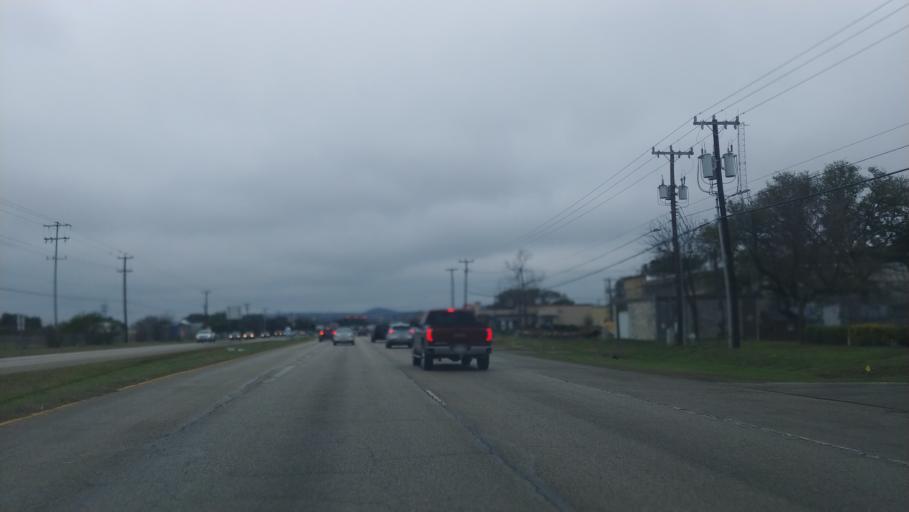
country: US
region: Texas
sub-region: Bexar County
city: Helotes
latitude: 29.5621
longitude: -98.6826
